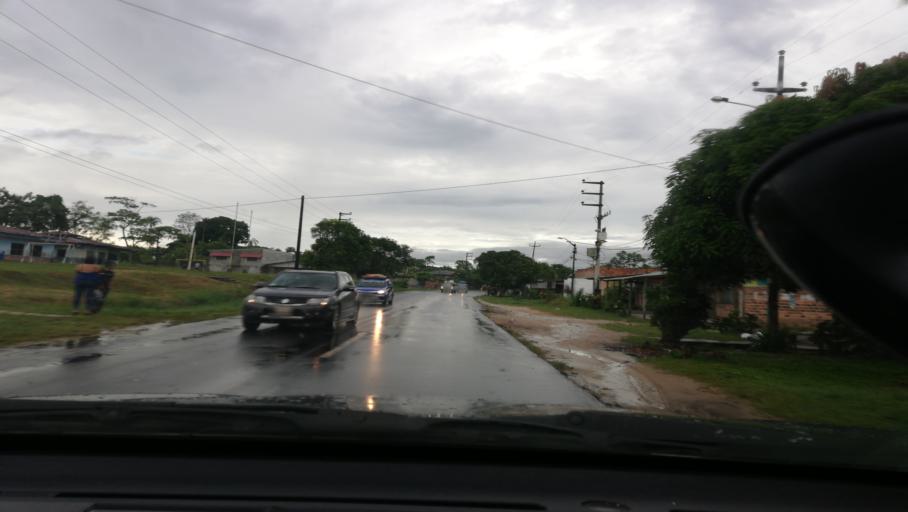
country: PE
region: Loreto
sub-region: Provincia de Maynas
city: Iquitos
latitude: -3.8627
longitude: -73.3371
